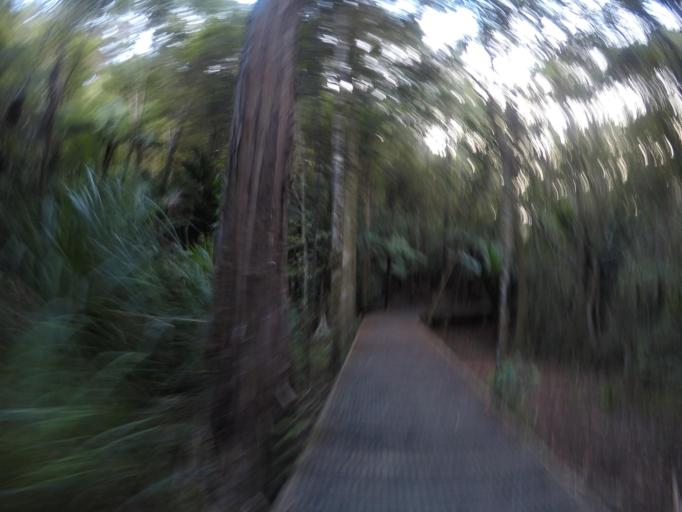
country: NZ
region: Auckland
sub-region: Auckland
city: North Shore
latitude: -36.7951
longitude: 174.7159
